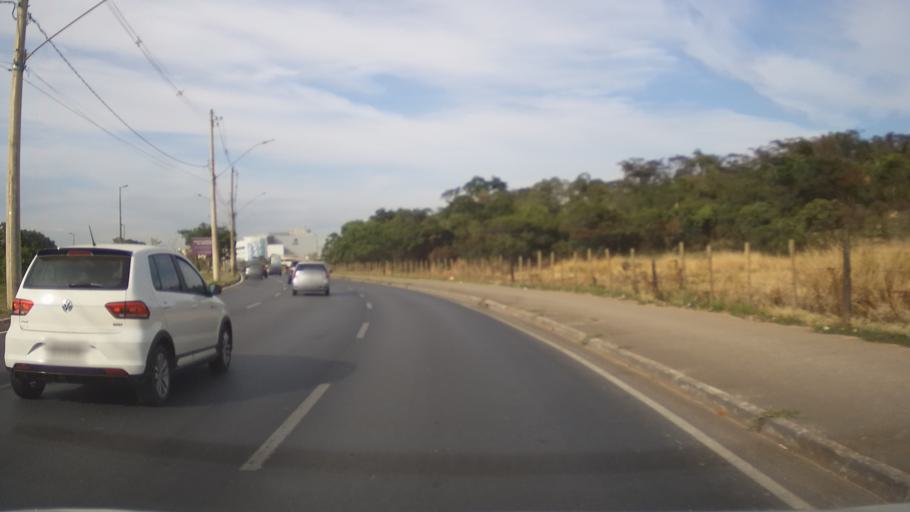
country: BR
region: Minas Gerais
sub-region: Contagem
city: Contagem
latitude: -19.8750
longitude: -44.0329
